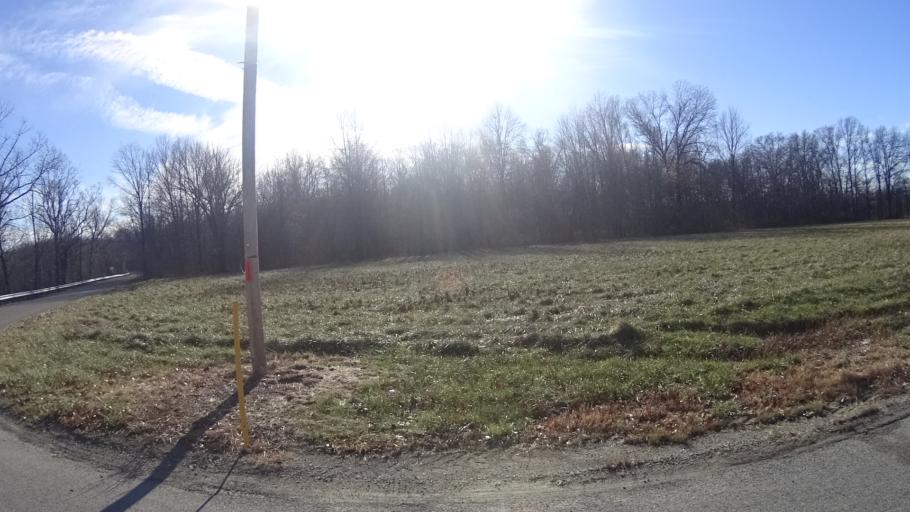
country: US
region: Ohio
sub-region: Lorain County
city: Vermilion-on-the-Lake
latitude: 41.3909
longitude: -82.3310
